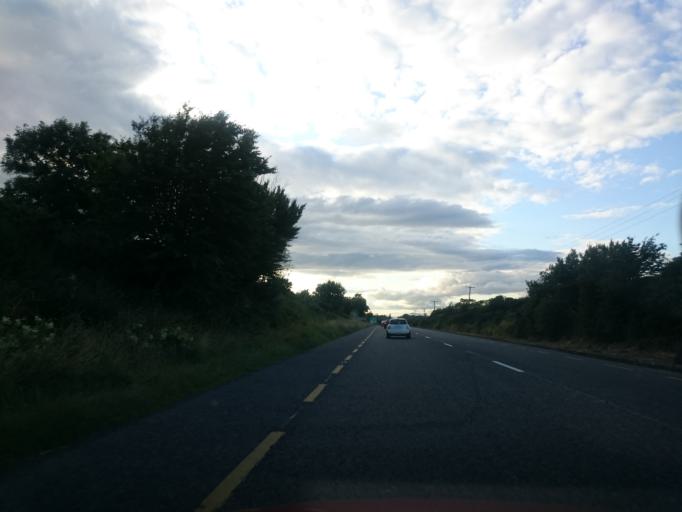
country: IE
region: Leinster
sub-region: Loch Garman
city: Loch Garman
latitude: 52.3180
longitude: -6.4958
